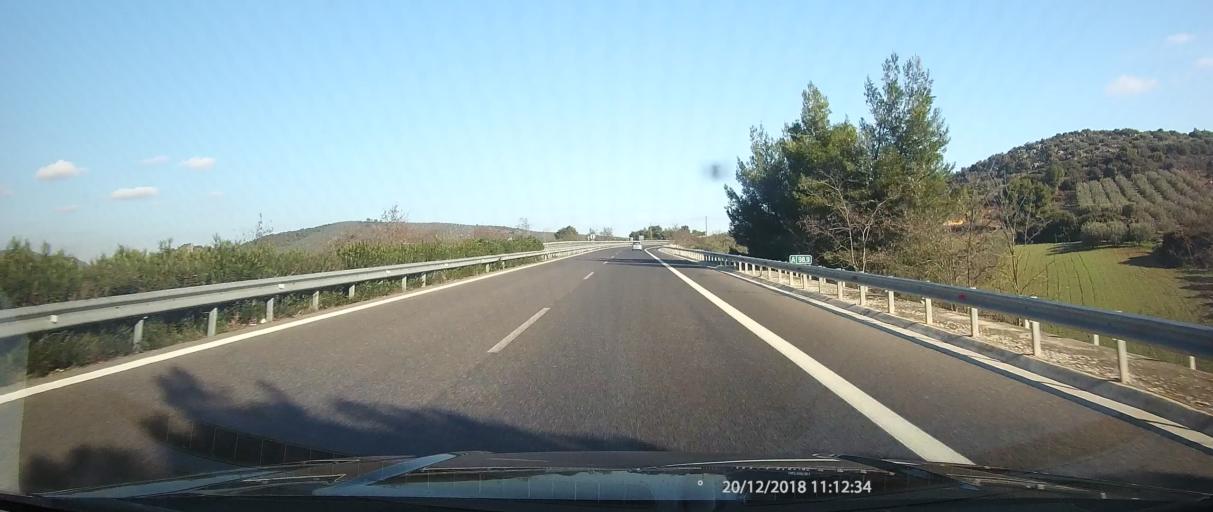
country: GR
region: Peloponnese
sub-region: Nomos Korinthias
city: Ayios Vasilios
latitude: 37.8423
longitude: 22.8126
